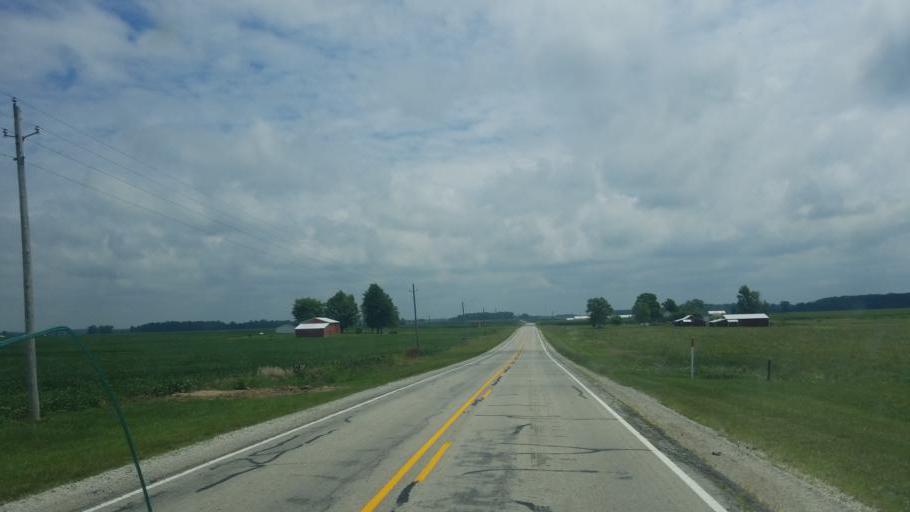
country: US
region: Indiana
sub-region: Huntington County
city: Warren
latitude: 40.6680
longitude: -85.4783
